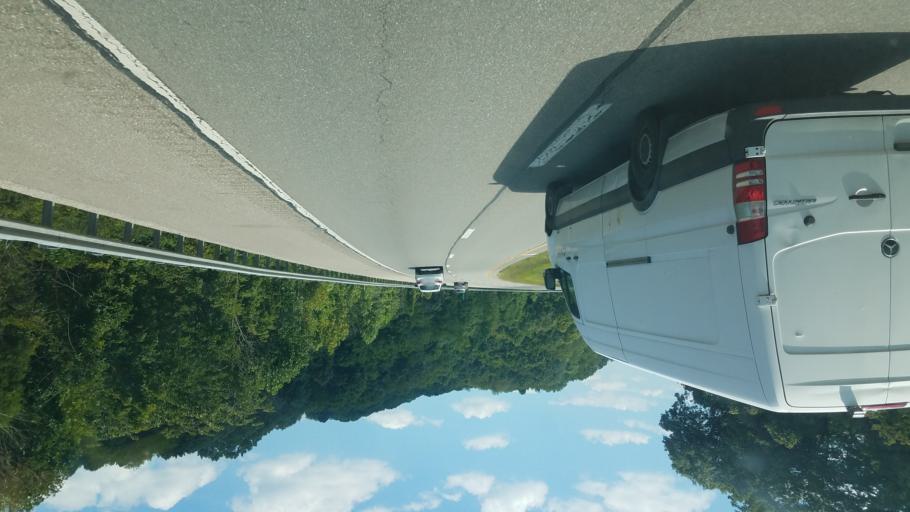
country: US
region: West Virginia
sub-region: Kanawha County
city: Charleston
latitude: 38.4014
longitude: -81.6173
